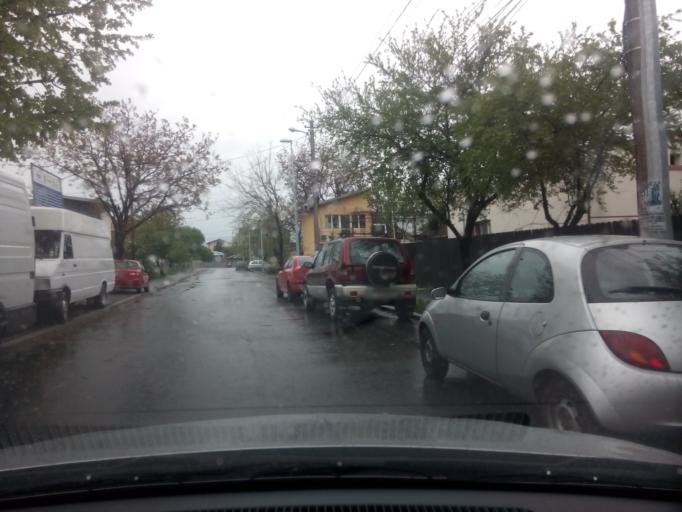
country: RO
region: Ilfov
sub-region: Voluntari City
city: Voluntari
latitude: 44.4853
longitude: 26.1669
